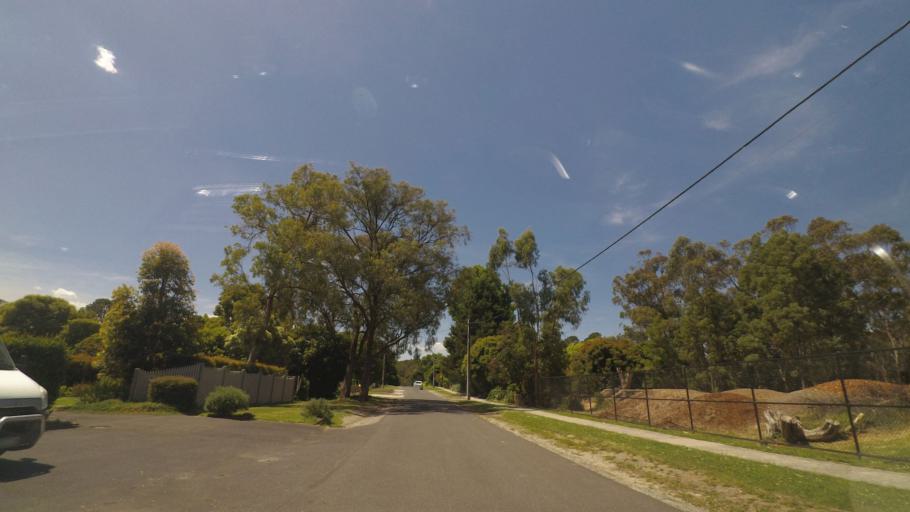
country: AU
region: Victoria
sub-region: Yarra Ranges
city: Montrose
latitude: -37.8070
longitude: 145.3436
